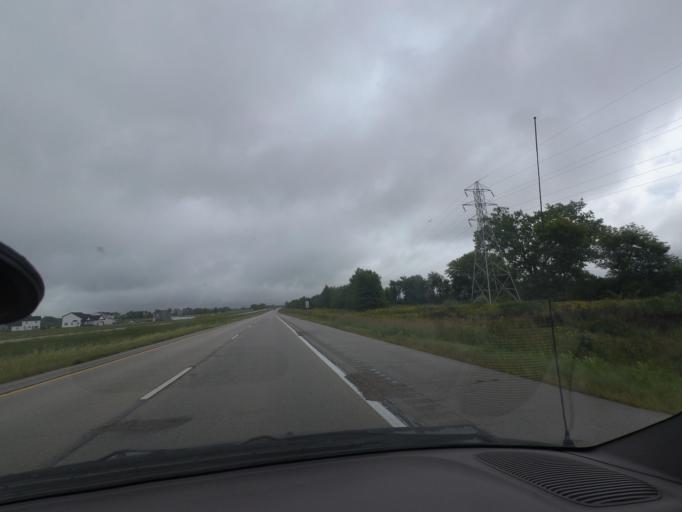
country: US
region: Illinois
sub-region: Piatt County
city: Monticello
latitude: 40.0594
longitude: -88.5553
